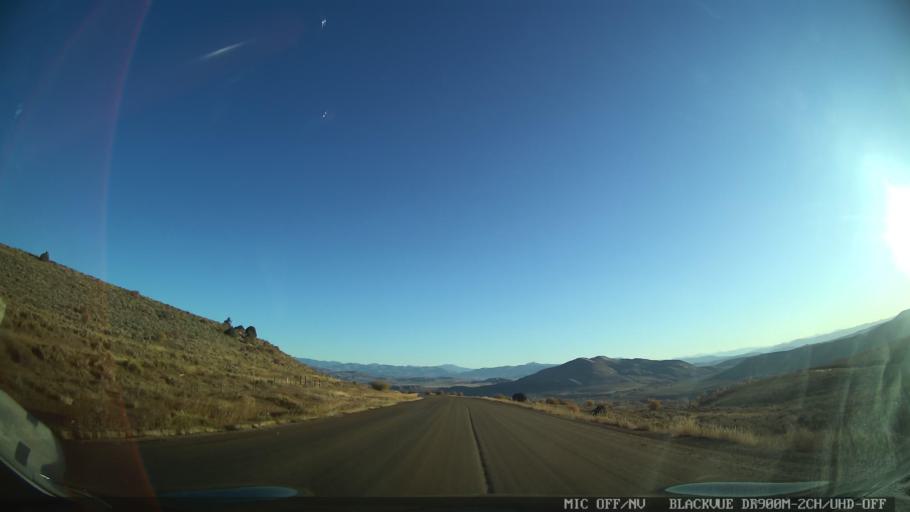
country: US
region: Colorado
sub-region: Grand County
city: Kremmling
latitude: 39.9977
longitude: -106.4087
